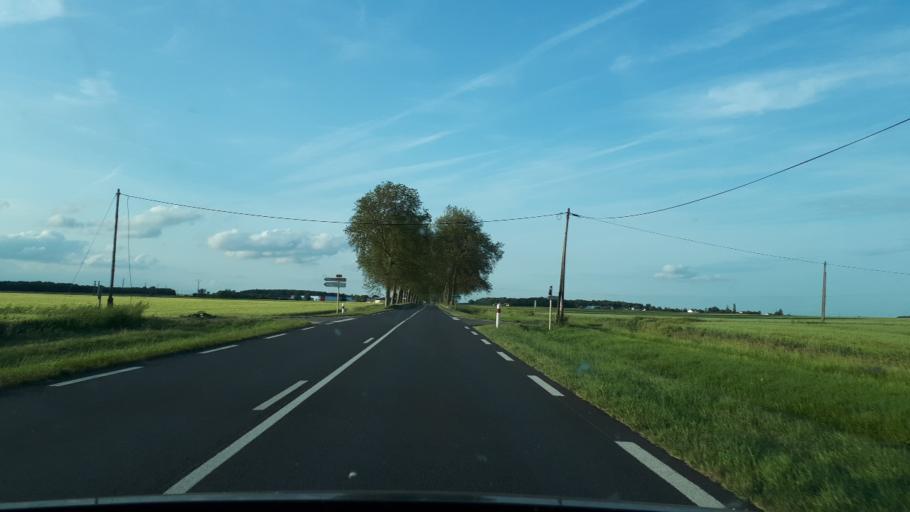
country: FR
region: Centre
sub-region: Departement du Loir-et-Cher
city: Naveil
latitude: 47.7540
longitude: 1.0455
